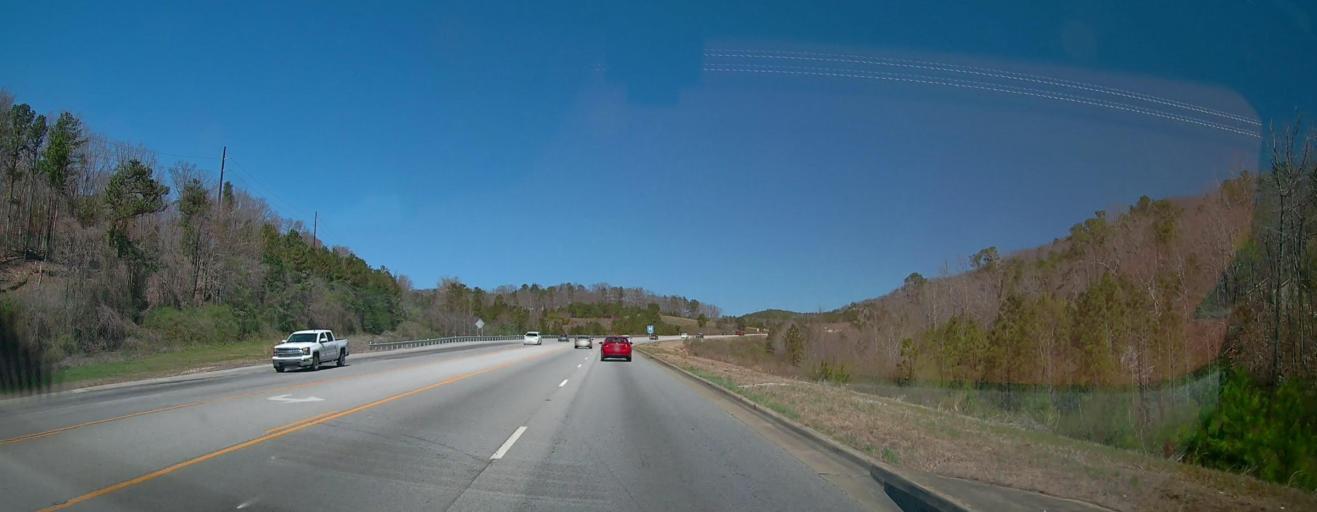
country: US
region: Alabama
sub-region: Calhoun County
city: Anniston
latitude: 33.6468
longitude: -85.7862
